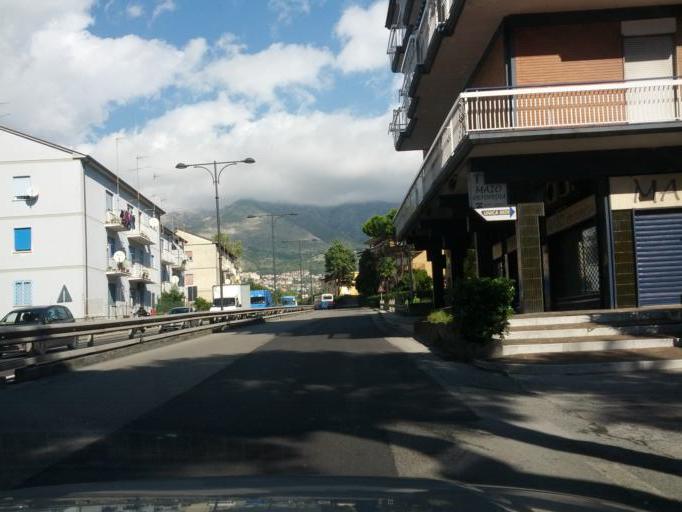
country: IT
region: Latium
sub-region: Provincia di Latina
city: Formia
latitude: 41.2620
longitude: 13.6201
